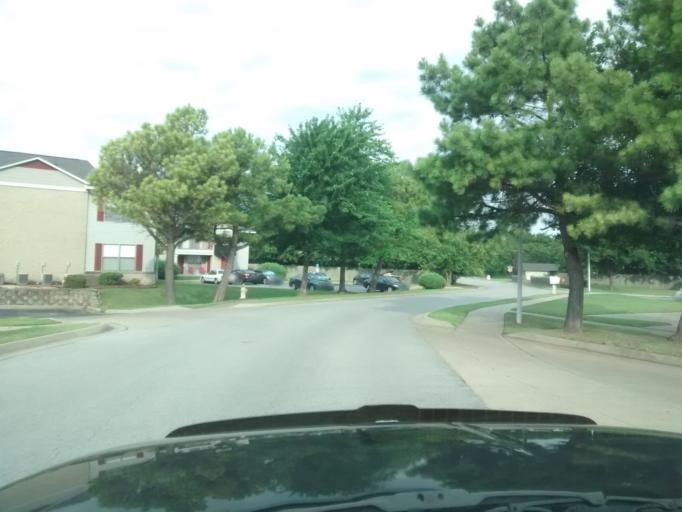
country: US
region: Arkansas
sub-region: Washington County
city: Fayetteville
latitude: 36.0749
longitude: -94.2045
